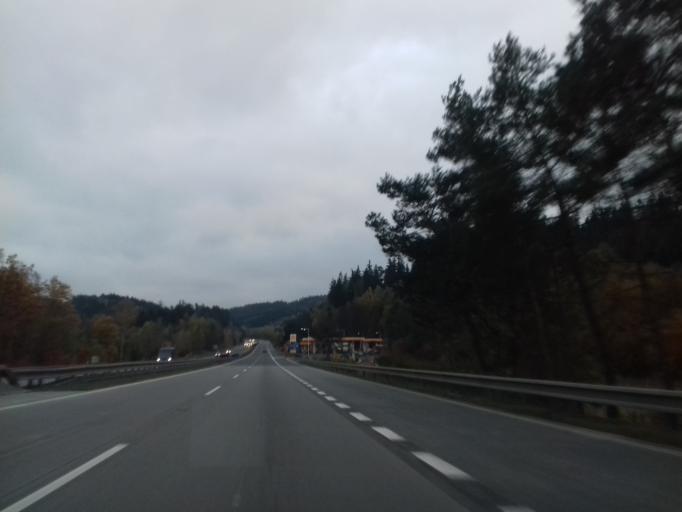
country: CZ
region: Central Bohemia
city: Divisov
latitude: 49.7826
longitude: 14.9311
